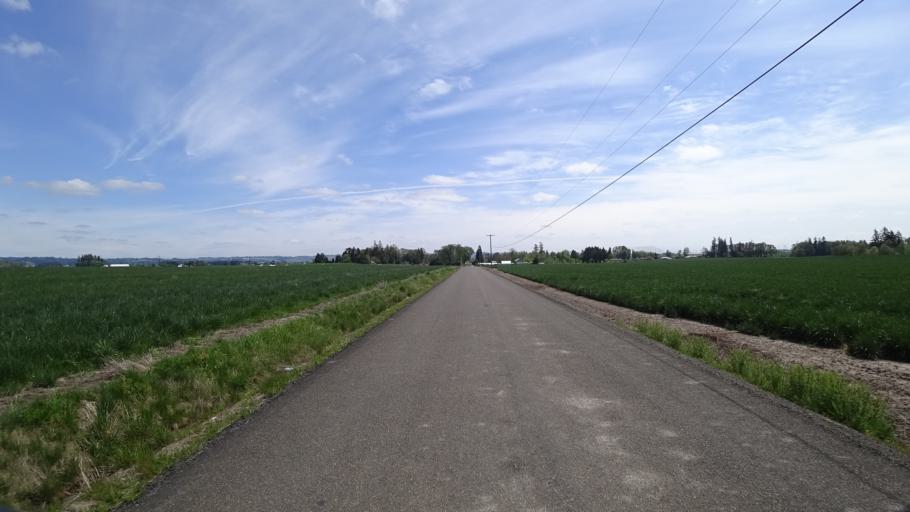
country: US
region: Oregon
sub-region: Washington County
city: North Plains
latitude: 45.5660
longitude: -122.9400
